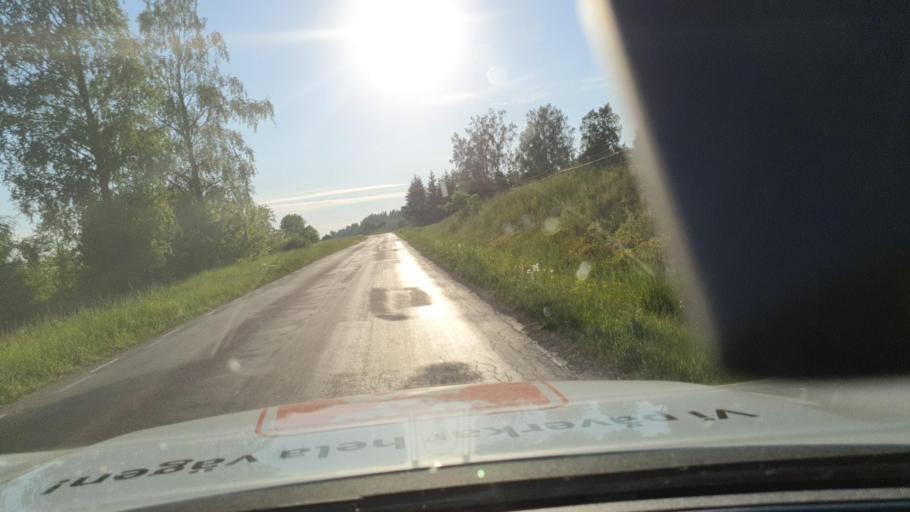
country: SE
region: Vaestra Goetaland
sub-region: Falkopings Kommun
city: Akarp
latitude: 58.0908
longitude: 13.6704
